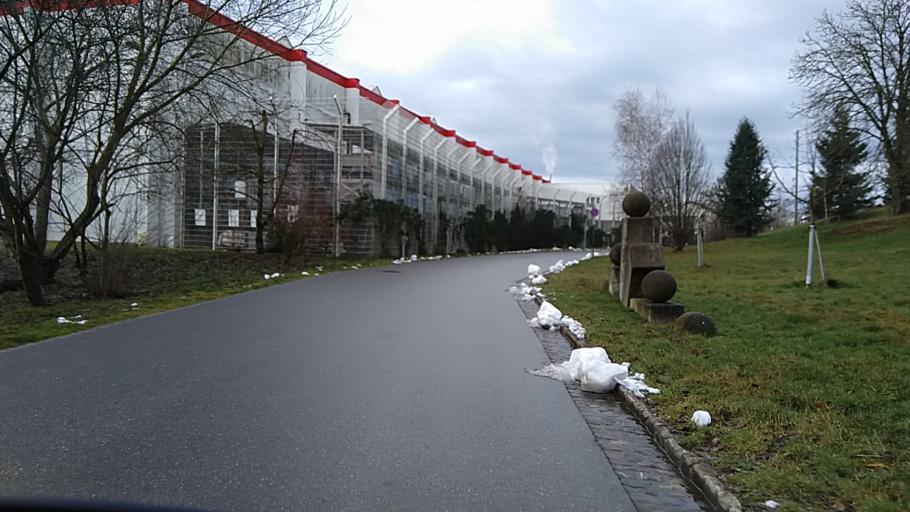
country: CH
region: Bern
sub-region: Bern-Mittelland District
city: Koniz
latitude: 46.9325
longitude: 7.3808
